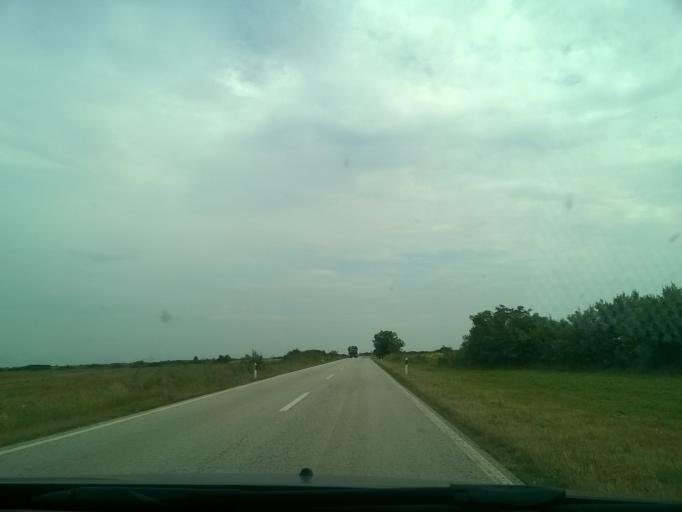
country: RS
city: Konak
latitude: 45.3298
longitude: 20.8880
